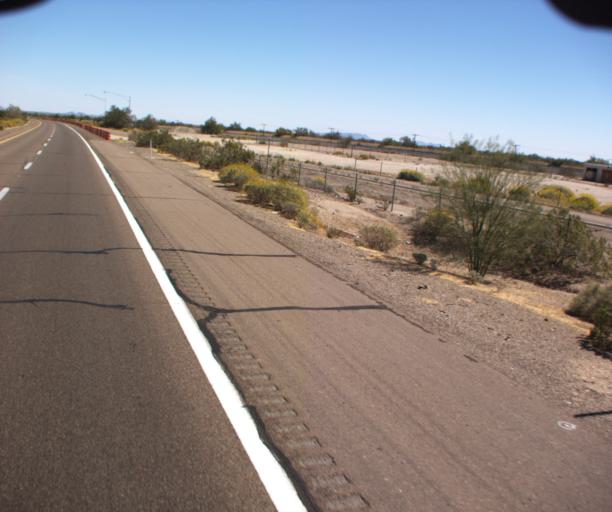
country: US
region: Arizona
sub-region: Yuma County
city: Wellton
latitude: 32.7307
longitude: -113.7159
